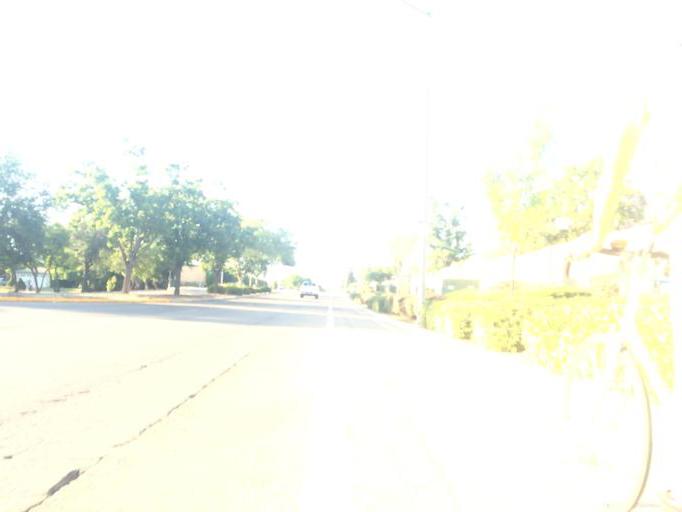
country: US
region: California
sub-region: Fresno County
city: Tarpey Village
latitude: 36.7912
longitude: -119.6821
